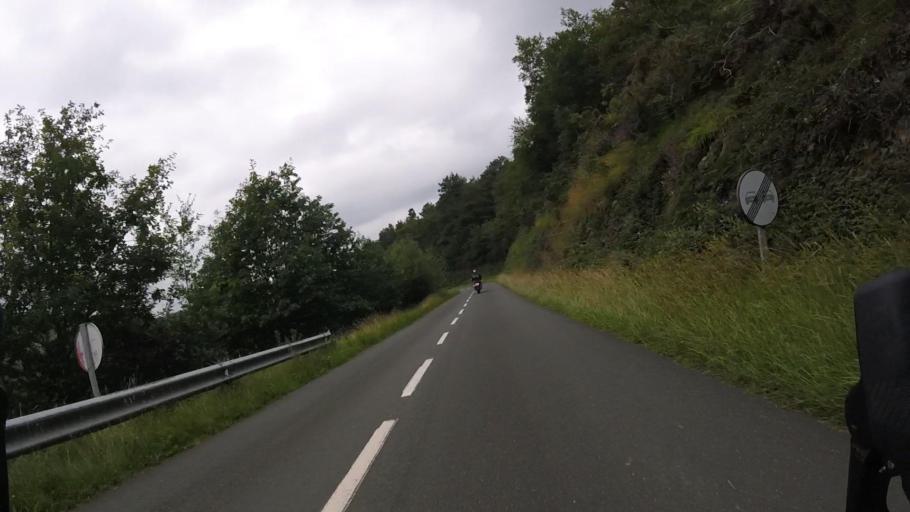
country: ES
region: Basque Country
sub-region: Provincia de Guipuzcoa
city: Irun
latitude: 43.2733
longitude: -1.8021
